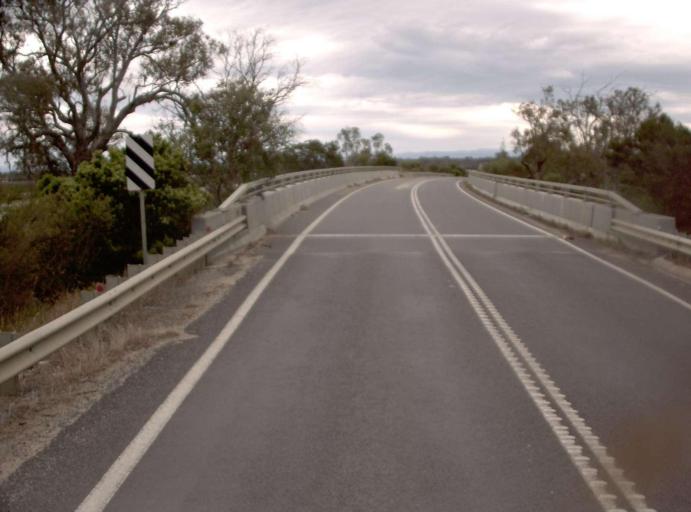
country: AU
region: Victoria
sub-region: Wellington
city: Sale
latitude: -38.1520
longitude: 147.0820
